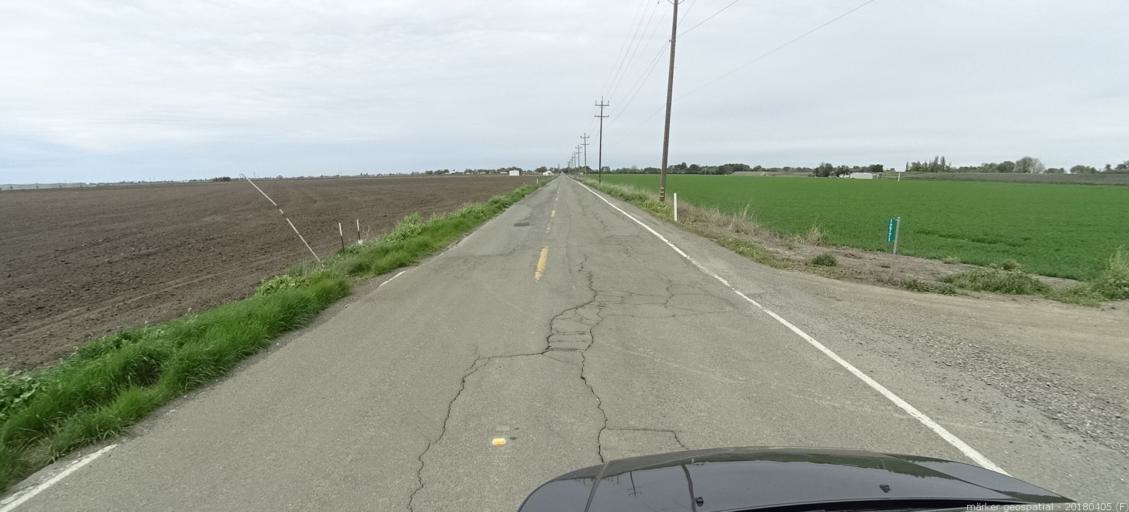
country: US
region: California
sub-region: Sacramento County
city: Walnut Grove
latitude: 38.2926
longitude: -121.5174
